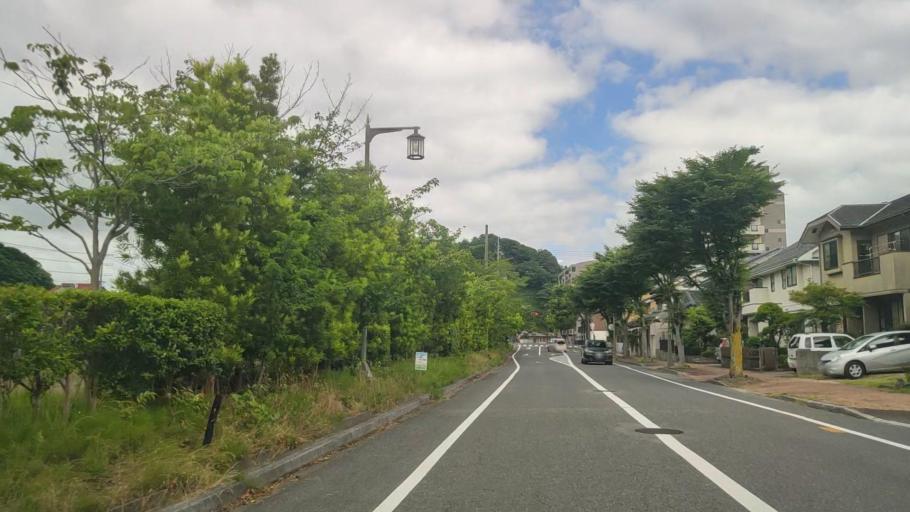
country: JP
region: Tottori
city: Yonago
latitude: 35.4221
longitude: 133.3313
